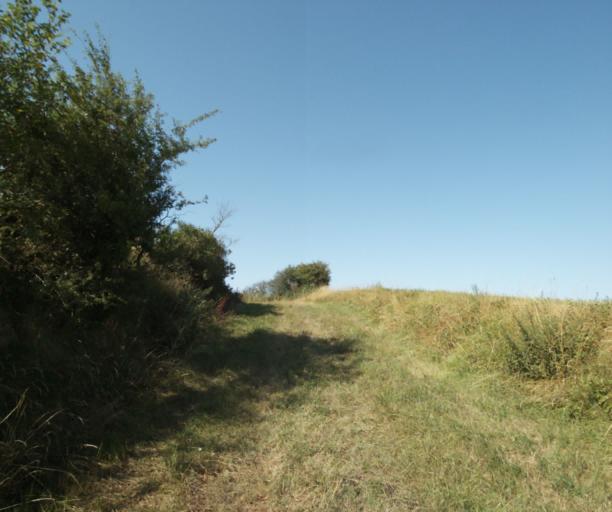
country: FR
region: Midi-Pyrenees
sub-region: Departement de la Haute-Garonne
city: Avignonet-Lauragais
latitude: 43.4223
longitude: 1.8236
